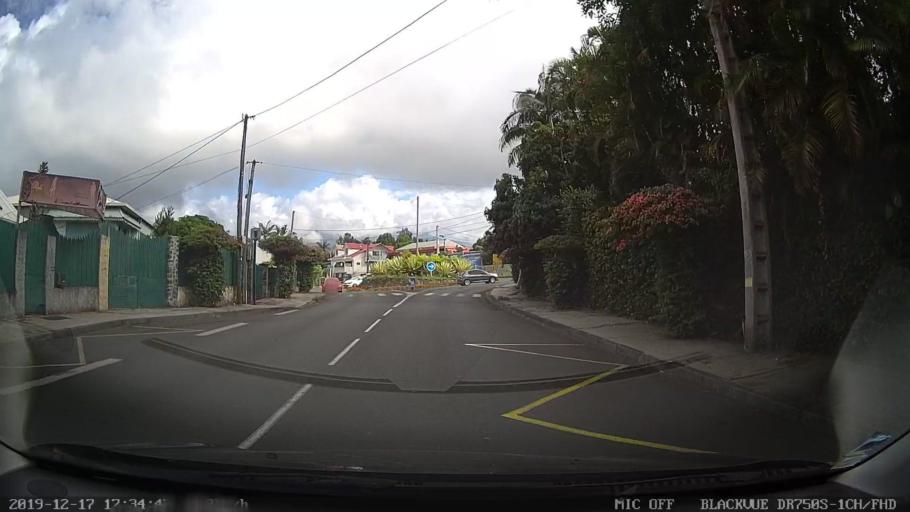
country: RE
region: Reunion
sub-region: Reunion
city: Le Tampon
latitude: -21.2686
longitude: 55.5105
